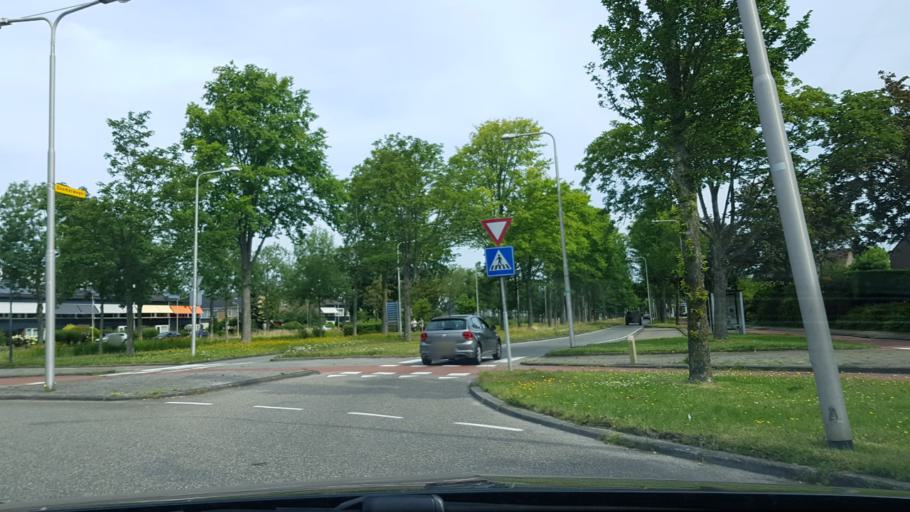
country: NL
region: North Holland
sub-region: Gemeente Castricum
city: Castricum
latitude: 52.5534
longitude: 4.6749
